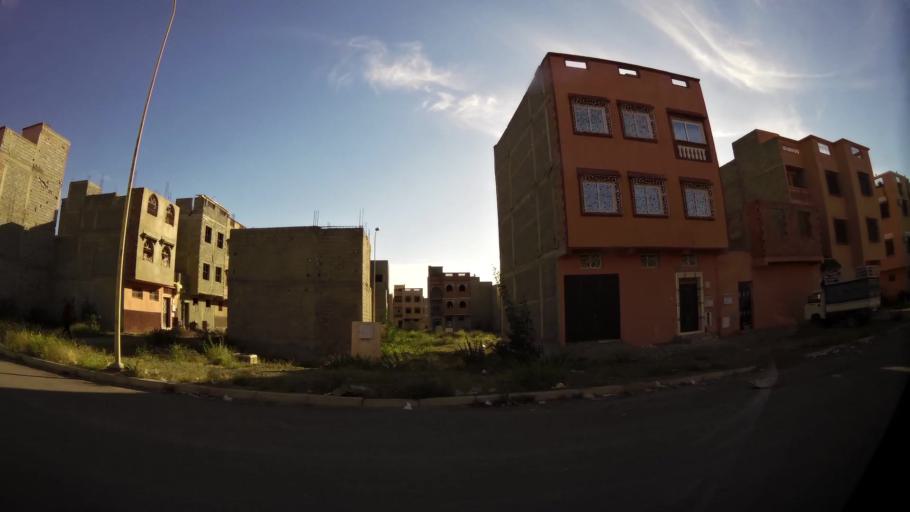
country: MA
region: Marrakech-Tensift-Al Haouz
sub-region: Marrakech
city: Marrakesh
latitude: 31.7596
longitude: -8.1008
